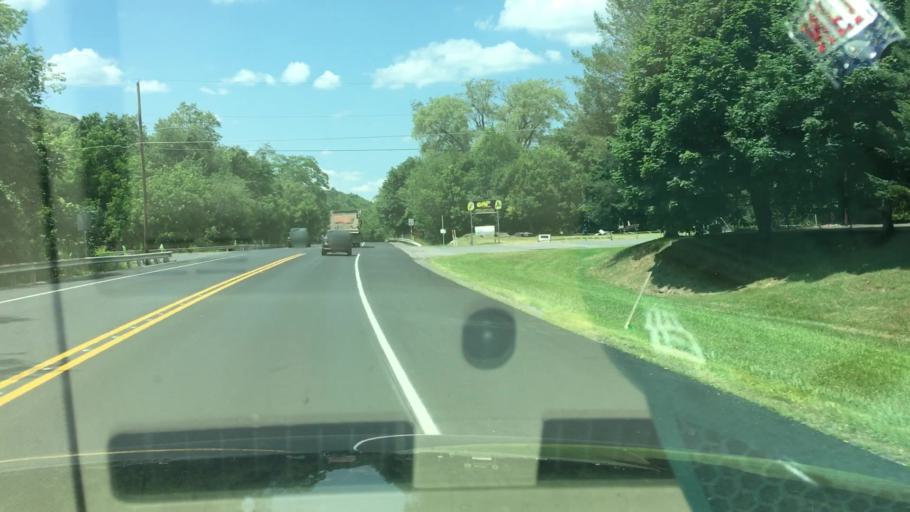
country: US
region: Pennsylvania
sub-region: Northumberland County
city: Kulpmont
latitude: 40.7709
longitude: -76.4413
